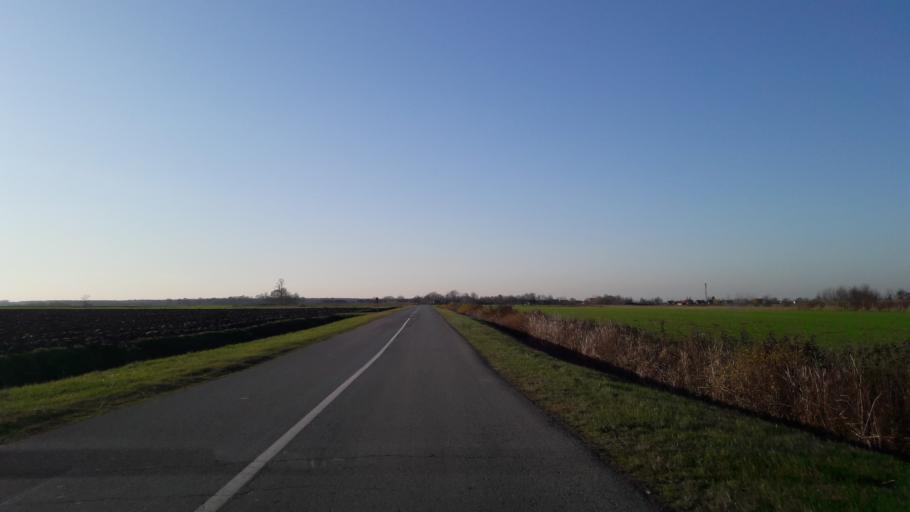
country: HR
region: Osjecko-Baranjska
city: Vuka
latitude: 45.4224
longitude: 18.5136
